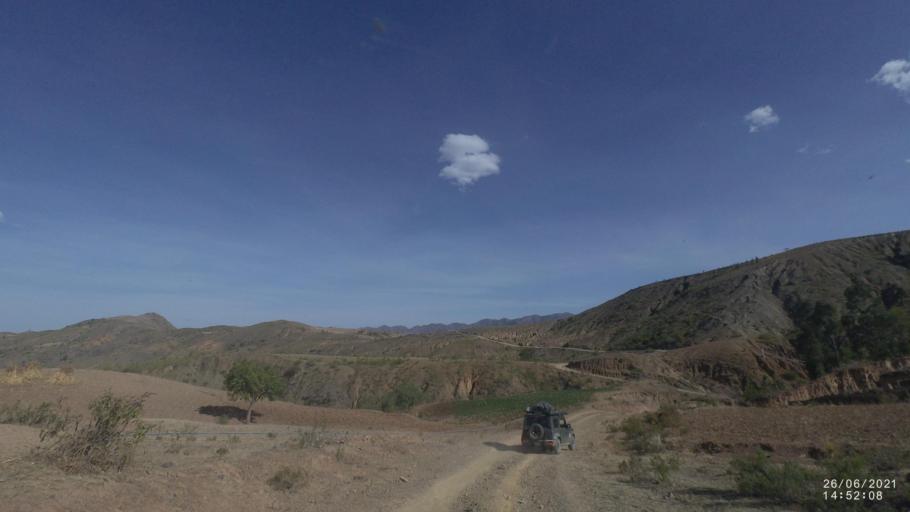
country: BO
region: Cochabamba
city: Mizque
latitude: -17.9256
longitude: -65.6272
